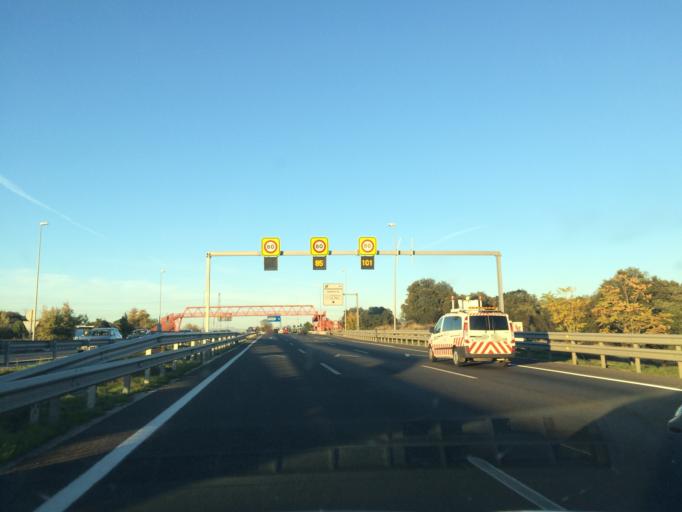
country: ES
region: Madrid
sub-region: Provincia de Madrid
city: Tres Cantos
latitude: 40.5764
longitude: -3.7072
